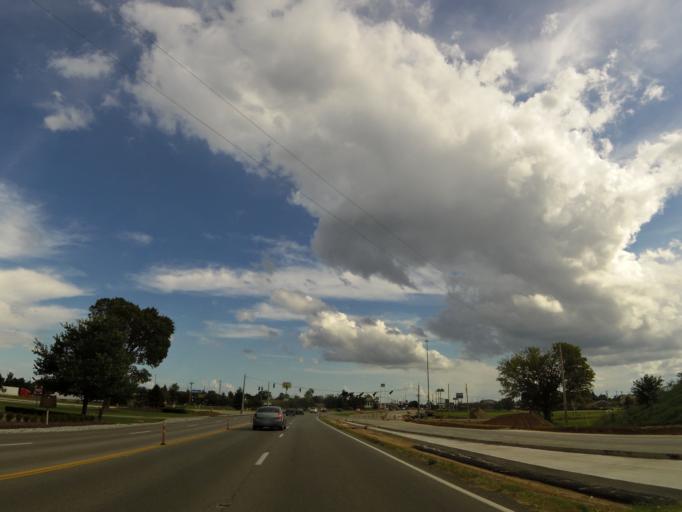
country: US
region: Kentucky
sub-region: Christian County
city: Hopkinsville
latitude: 36.8317
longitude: -87.4731
